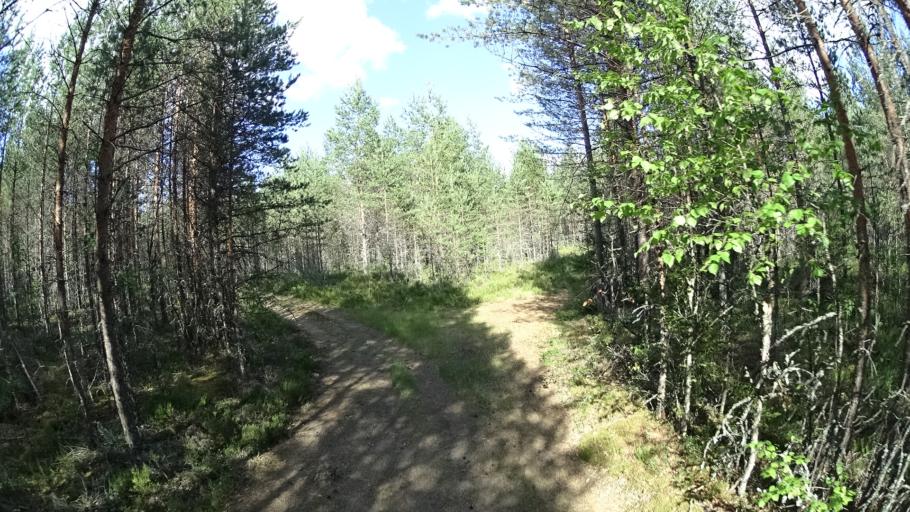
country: FI
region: Uusimaa
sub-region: Helsinki
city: Kaerkoelae
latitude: 60.7328
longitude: 24.0577
